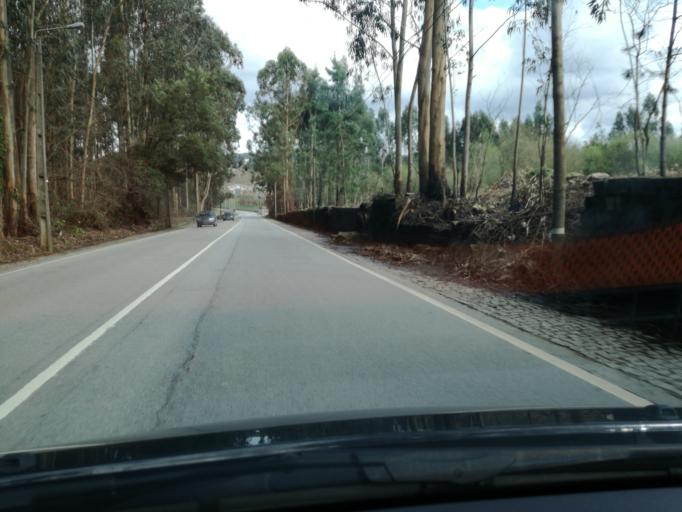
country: PT
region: Porto
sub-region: Maia
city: Nogueira
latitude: 41.2560
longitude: -8.5649
